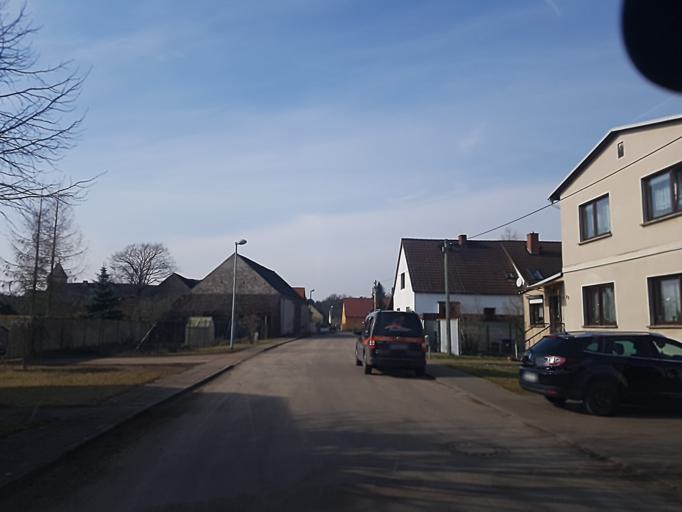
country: DE
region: Brandenburg
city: Wenzlow
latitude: 52.3263
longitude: 12.4422
